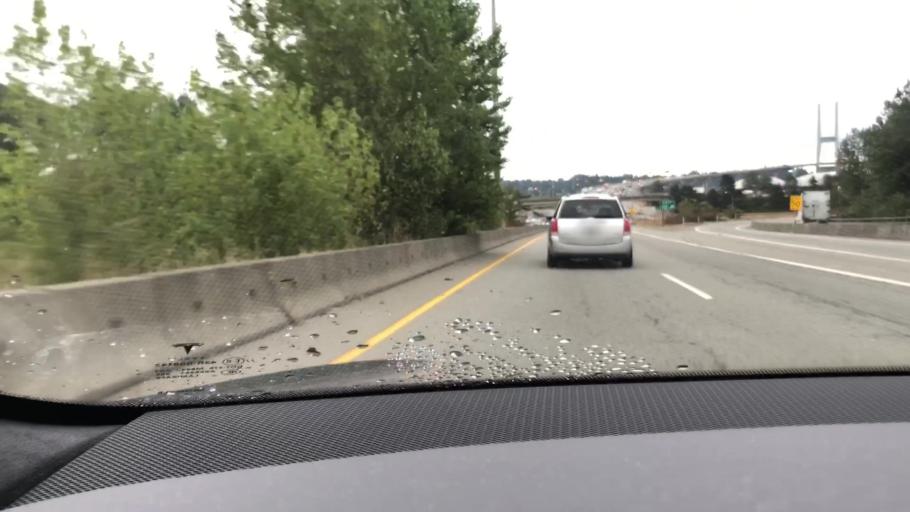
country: CA
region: British Columbia
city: New Westminster
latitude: 49.1733
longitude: -122.9556
